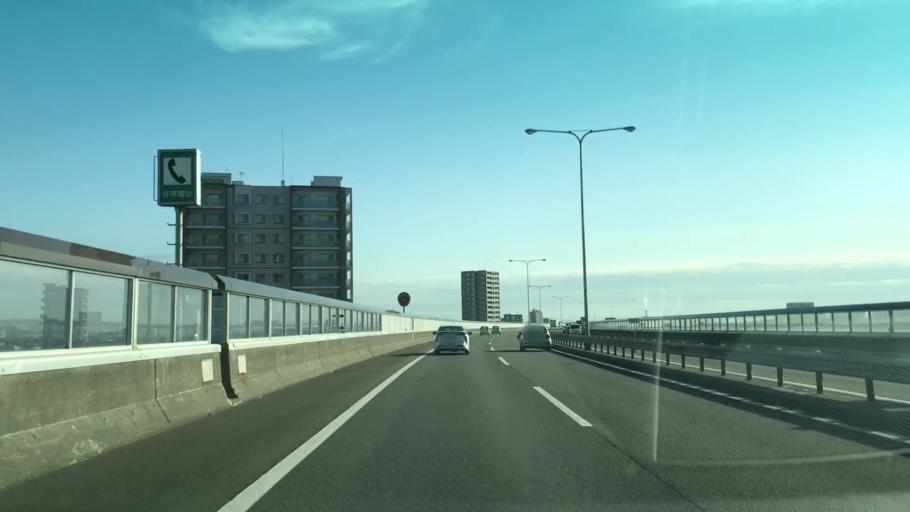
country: JP
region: Hokkaido
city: Sapporo
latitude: 43.1045
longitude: 141.3720
